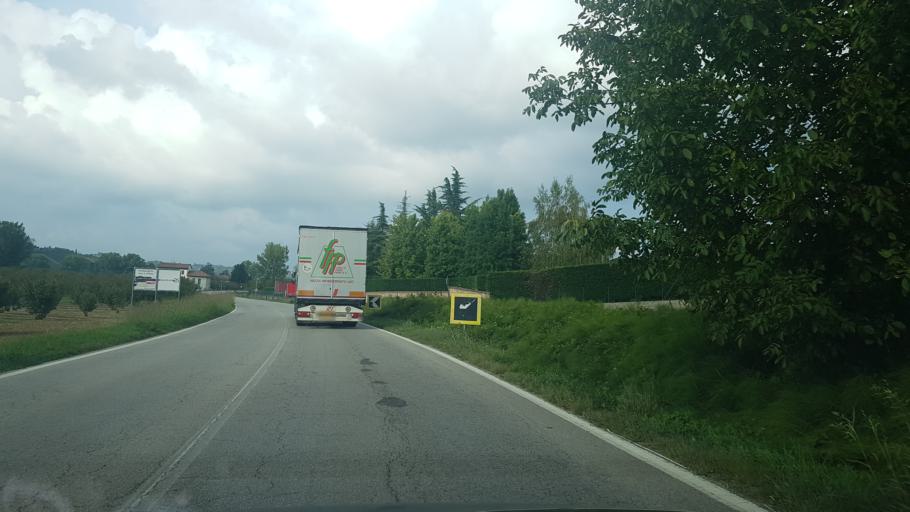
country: IT
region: Piedmont
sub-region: Provincia di Asti
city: Calamandrana
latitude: 44.7473
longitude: 8.3448
